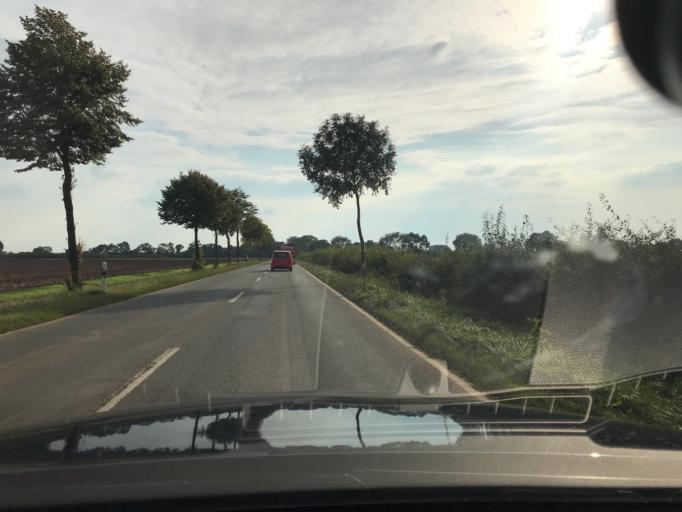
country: DE
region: Lower Saxony
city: Riede
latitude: 52.9955
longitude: 8.8986
